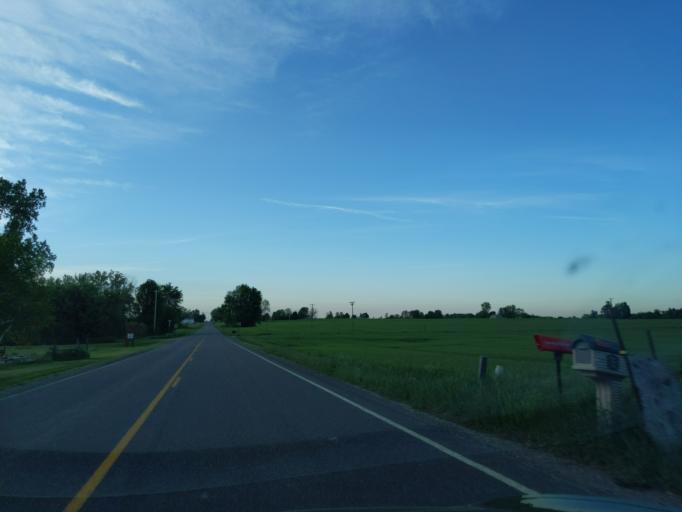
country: US
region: Michigan
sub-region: Ingham County
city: Williamston
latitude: 42.5764
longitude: -84.2985
